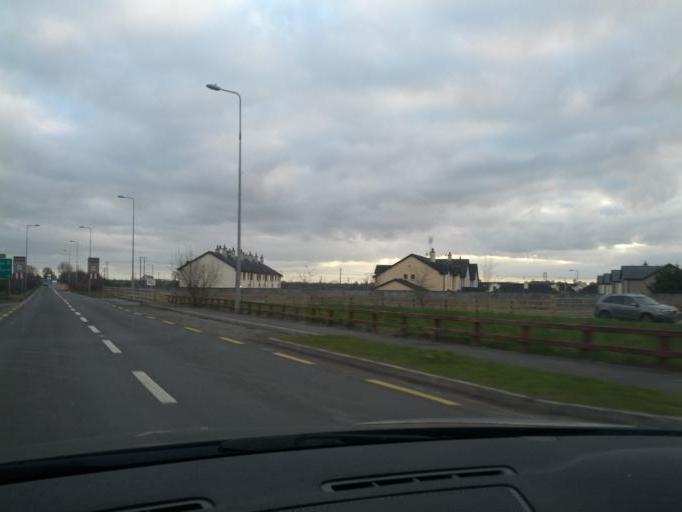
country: IE
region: Leinster
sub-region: Uibh Fhaili
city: Ferbane
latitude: 53.2223
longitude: -7.8853
